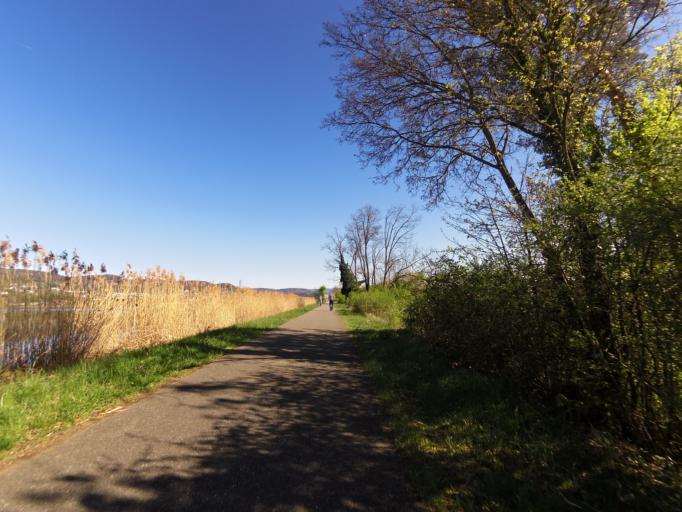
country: CH
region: Aargau
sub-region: Bezirk Zurzach
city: Klingnau
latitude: 47.5864
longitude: 8.2296
